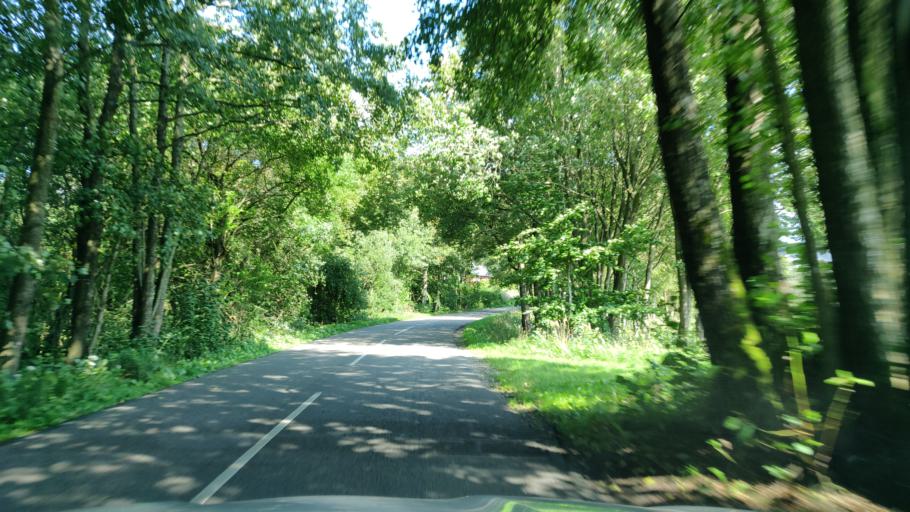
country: DK
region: Central Jutland
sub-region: Herning Kommune
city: Avlum
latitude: 56.2454
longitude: 8.8748
